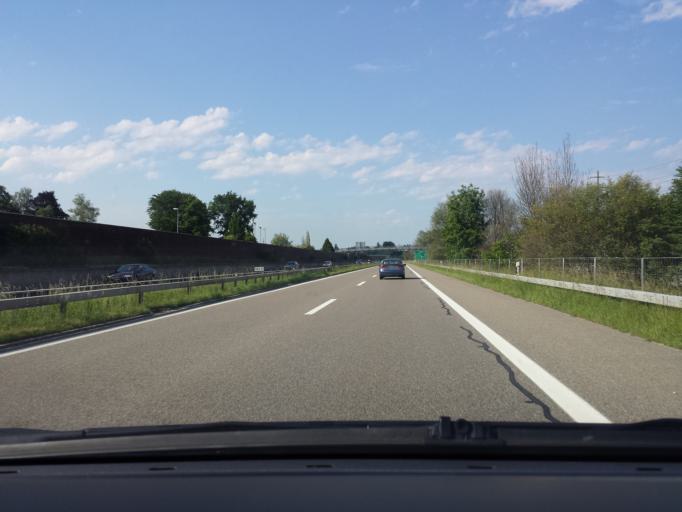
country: CH
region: Saint Gallen
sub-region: Wahlkreis Rheintal
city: Diepoldsau
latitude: 47.3979
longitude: 9.6467
